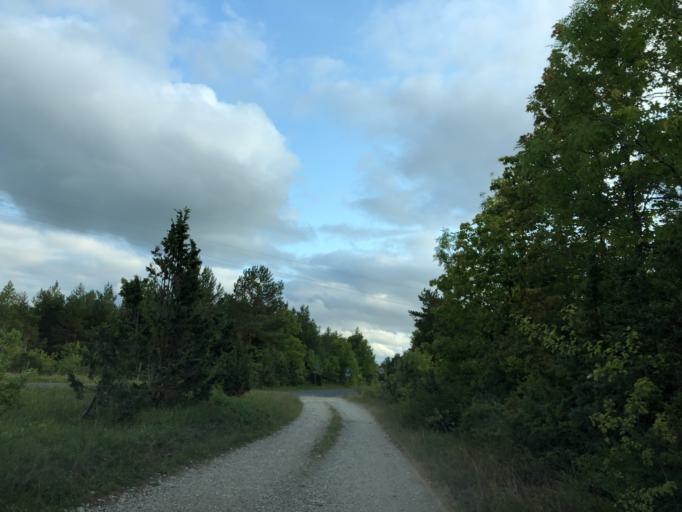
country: EE
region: Hiiumaa
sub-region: Kaerdla linn
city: Kardla
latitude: 58.7890
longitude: 22.8321
